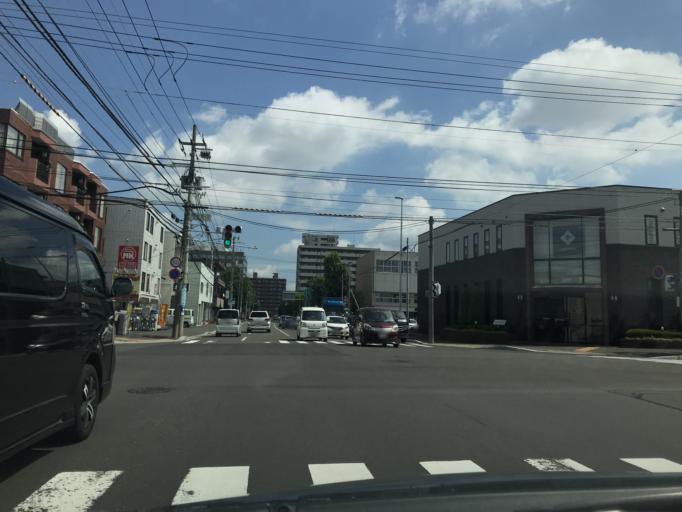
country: JP
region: Hokkaido
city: Sapporo
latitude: 43.0579
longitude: 141.3776
